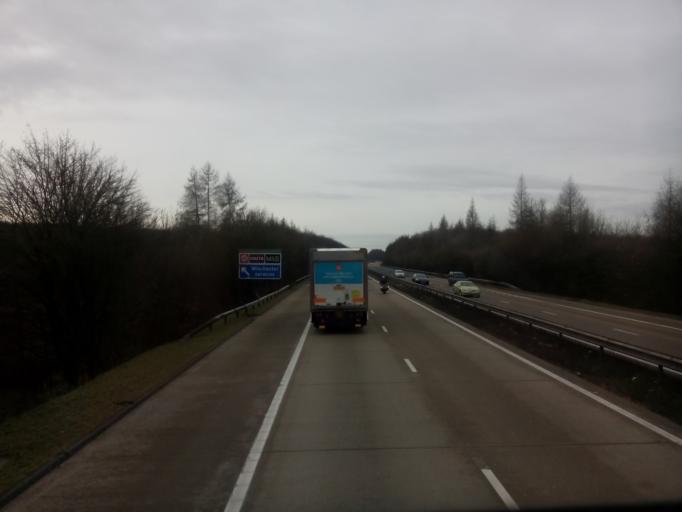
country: GB
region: England
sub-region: Hampshire
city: Kings Worthy
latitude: 51.1256
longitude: -1.2499
